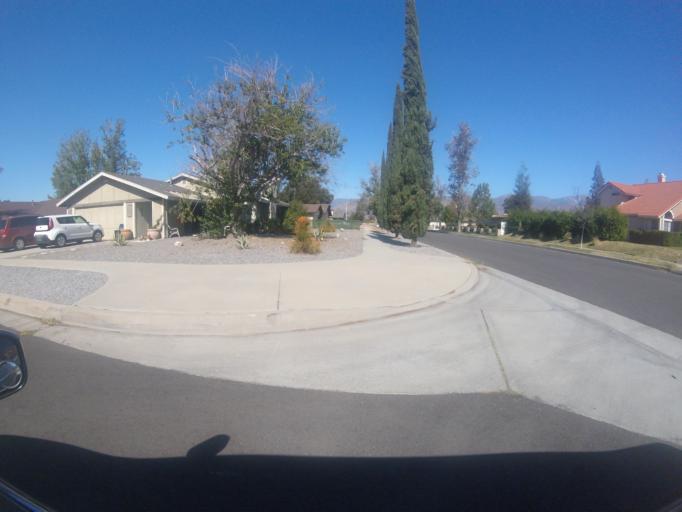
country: US
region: California
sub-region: San Bernardino County
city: Redlands
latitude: 34.0787
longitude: -117.1695
